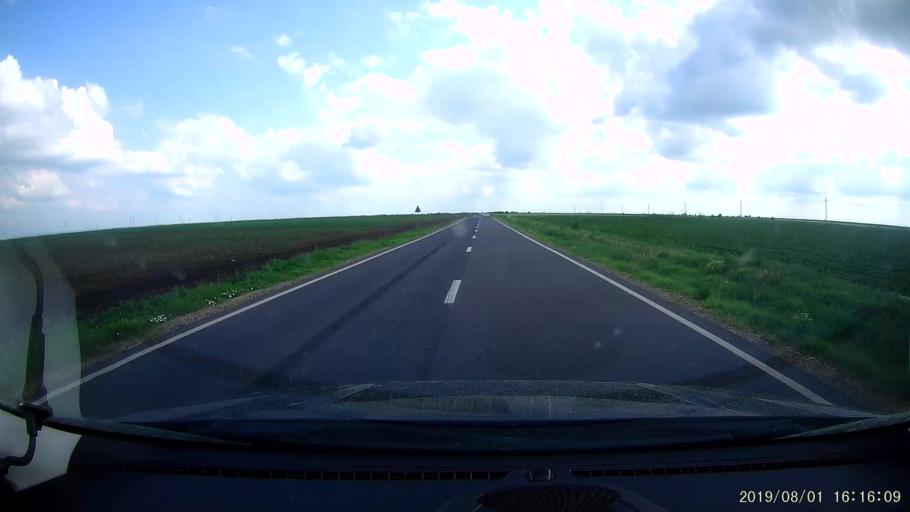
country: RO
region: Calarasi
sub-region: Comuna Stefan Voda
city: Stefan Voda
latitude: 44.3254
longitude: 27.3590
